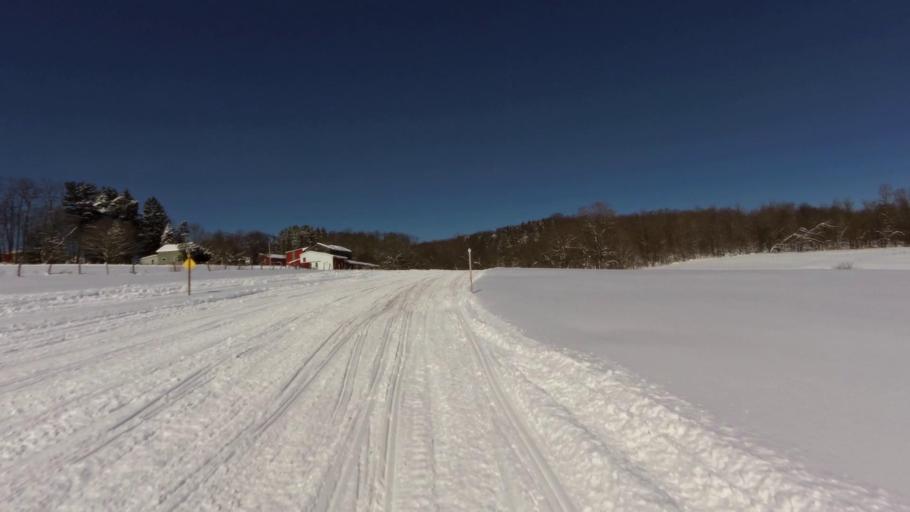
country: US
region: New York
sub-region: Chautauqua County
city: Mayville
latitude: 42.2523
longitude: -79.4409
